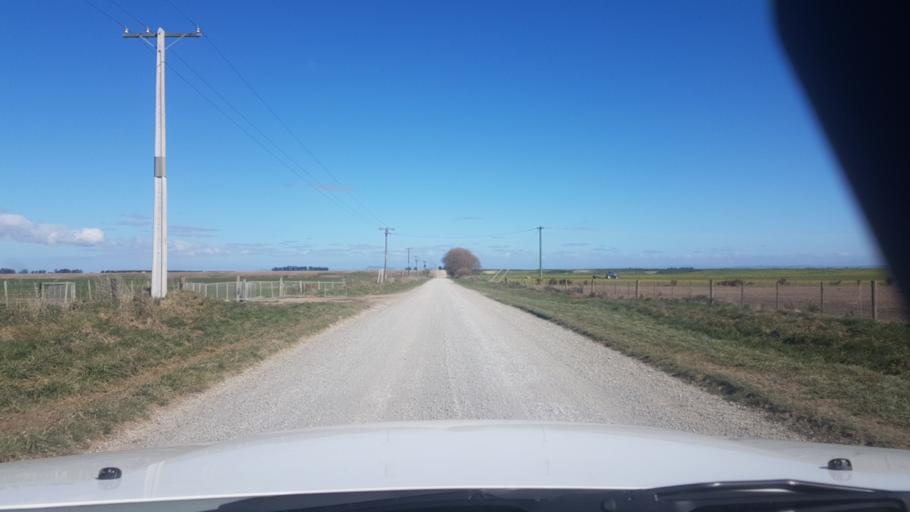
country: NZ
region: Canterbury
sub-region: Timaru District
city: Pleasant Point
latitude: -44.1199
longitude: 171.4133
